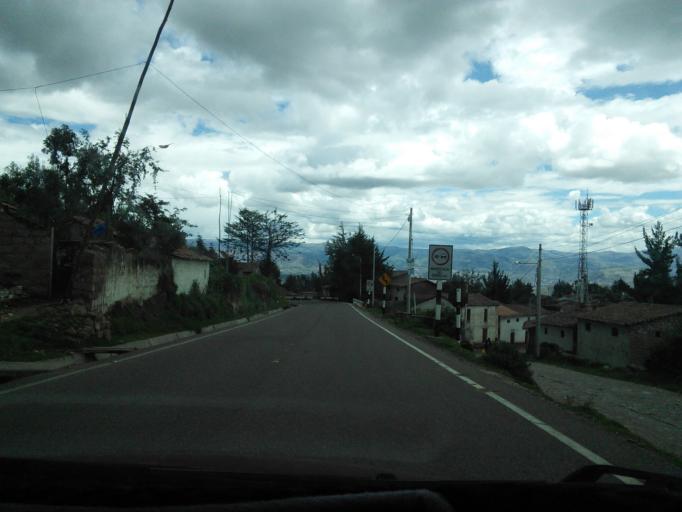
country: PE
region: Ayacucho
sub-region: Provincia de Huamanga
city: Quinua
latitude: -13.0475
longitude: -74.1360
